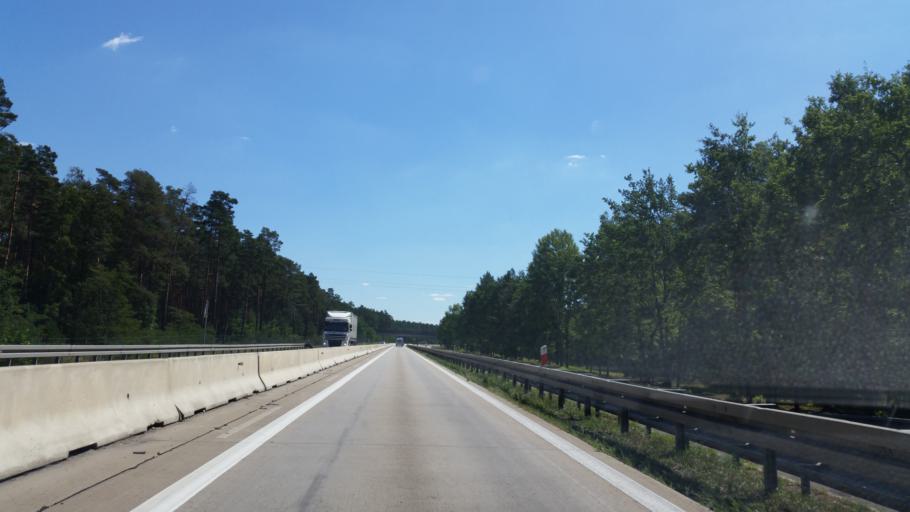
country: PL
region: Lubusz
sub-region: Powiat zaganski
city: Ilowa
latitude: 51.5217
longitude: 15.2235
